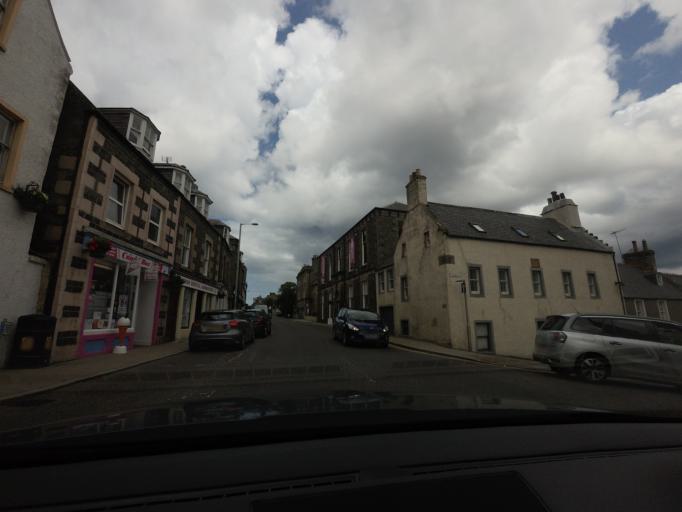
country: GB
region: Scotland
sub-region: Aberdeenshire
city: Banff
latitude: 57.6631
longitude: -2.5233
